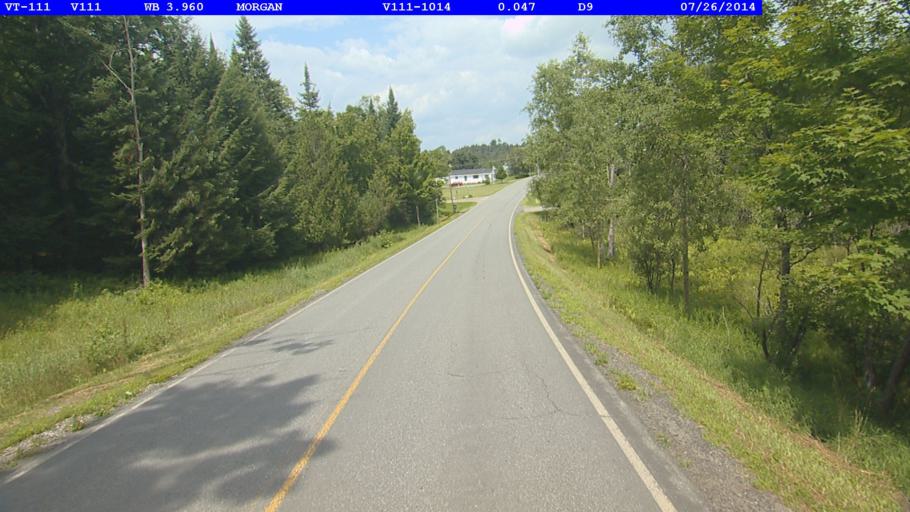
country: US
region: Vermont
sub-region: Orleans County
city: Newport
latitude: 44.9304
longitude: -72.0631
